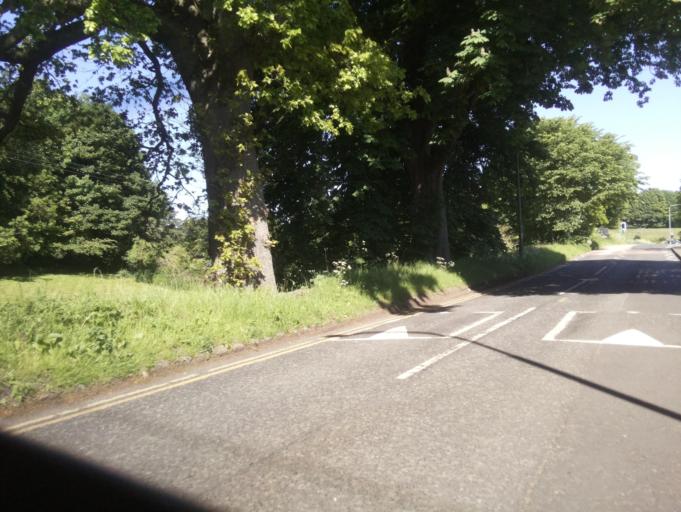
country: GB
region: Scotland
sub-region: Fife
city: Newport-On-Tay
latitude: 56.4317
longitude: -2.9364
